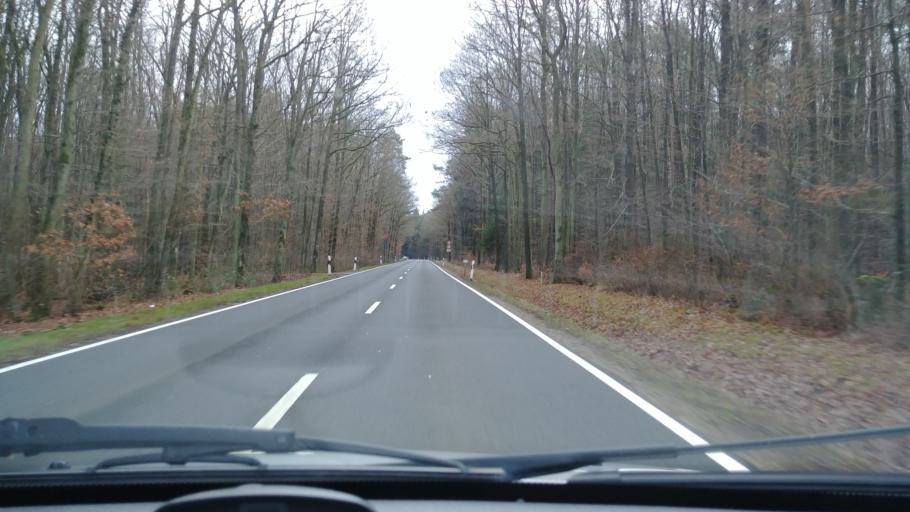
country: DE
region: Bavaria
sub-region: Regierungsbezirk Unterfranken
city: Erlenbach
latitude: 49.9996
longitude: 9.6300
